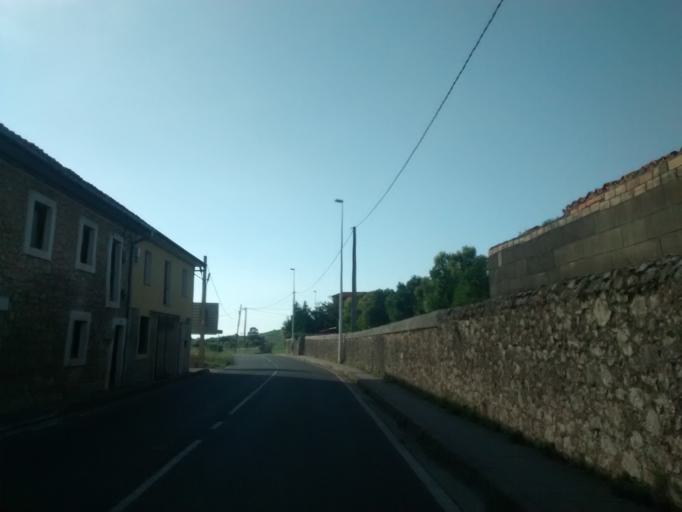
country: ES
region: Cantabria
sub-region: Provincia de Cantabria
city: Lierganes
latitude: 43.3991
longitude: -3.7354
